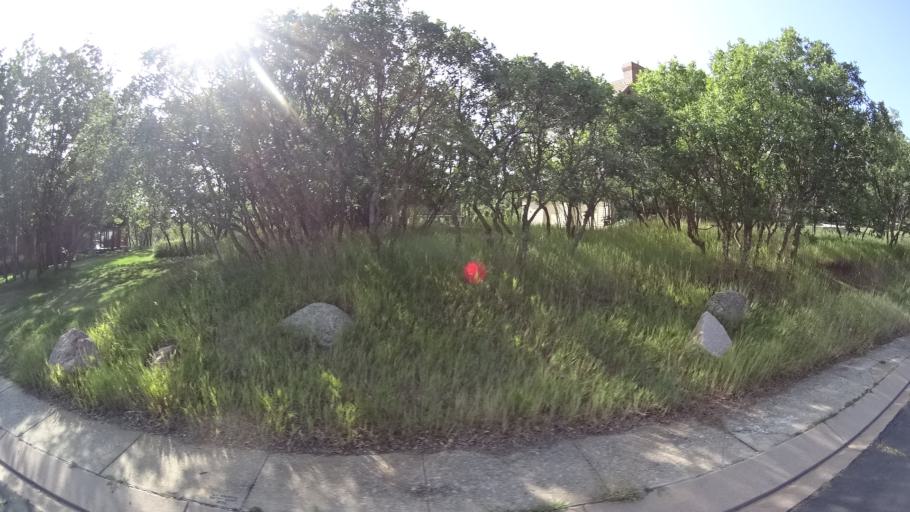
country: US
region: Colorado
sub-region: El Paso County
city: Manitou Springs
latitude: 38.8211
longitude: -104.8784
